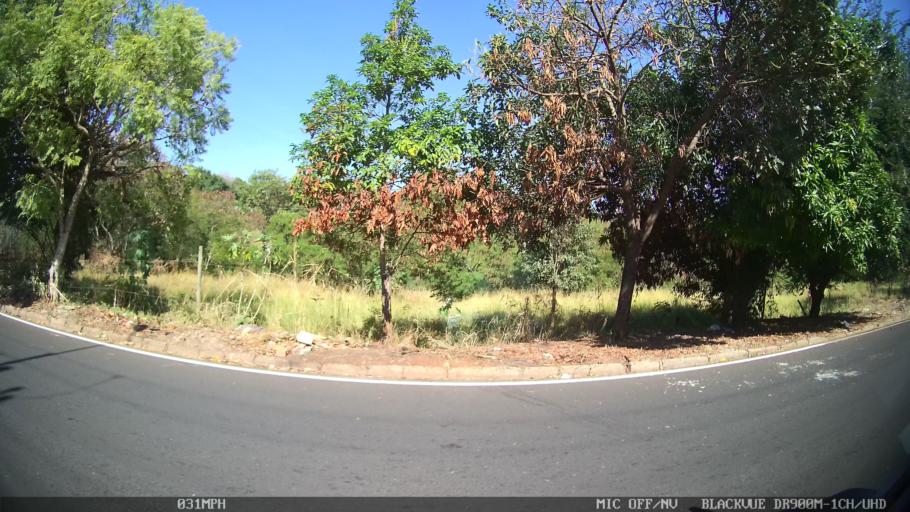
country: BR
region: Sao Paulo
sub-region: Sao Jose Do Rio Preto
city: Sao Jose do Rio Preto
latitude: -20.7728
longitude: -49.4060
